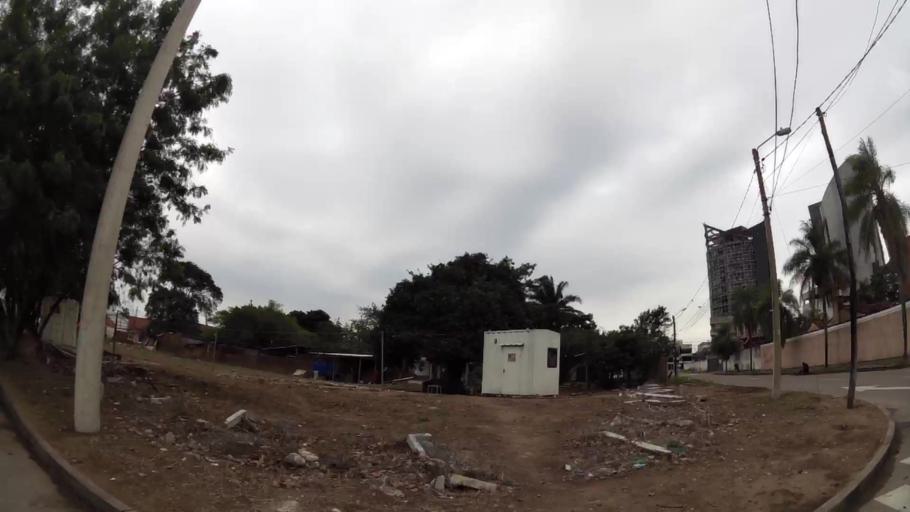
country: BO
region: Santa Cruz
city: Santa Cruz de la Sierra
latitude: -17.7608
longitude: -63.1768
